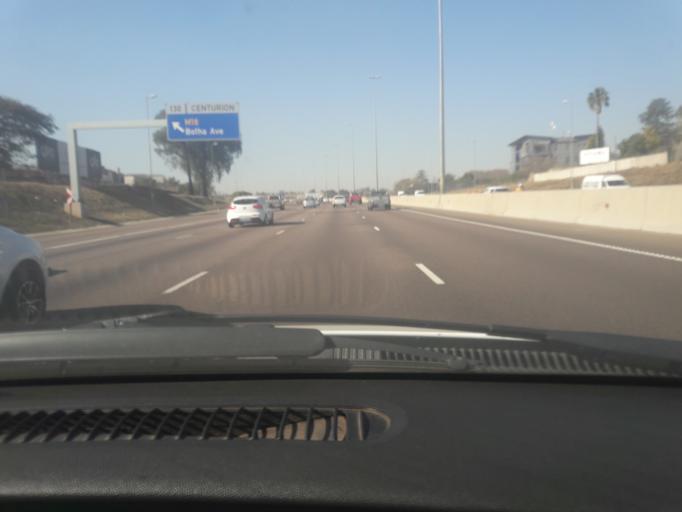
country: ZA
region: Gauteng
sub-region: City of Tshwane Metropolitan Municipality
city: Centurion
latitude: -25.8606
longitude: 28.2146
